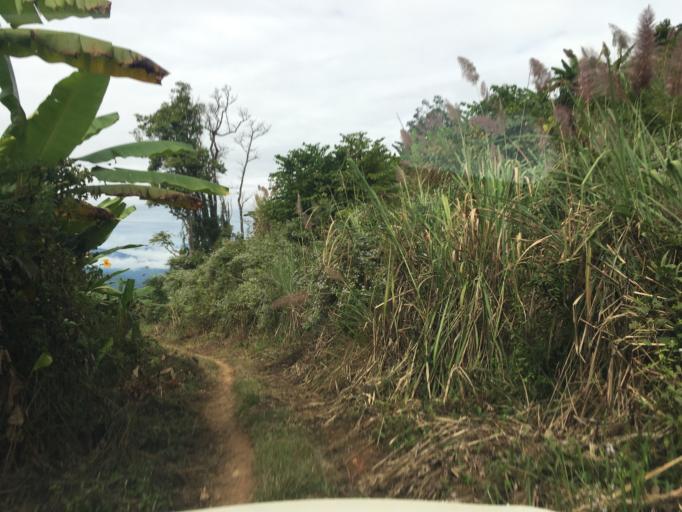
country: LA
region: Houaphan
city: Viengthong
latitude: 19.9148
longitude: 103.2998
